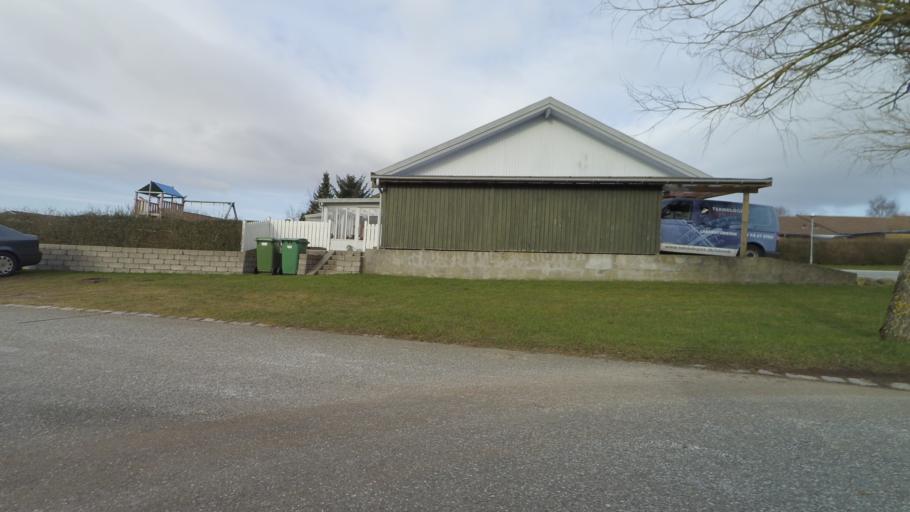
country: DK
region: Central Jutland
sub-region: Arhus Kommune
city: Kolt
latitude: 56.1055
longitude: 10.0789
